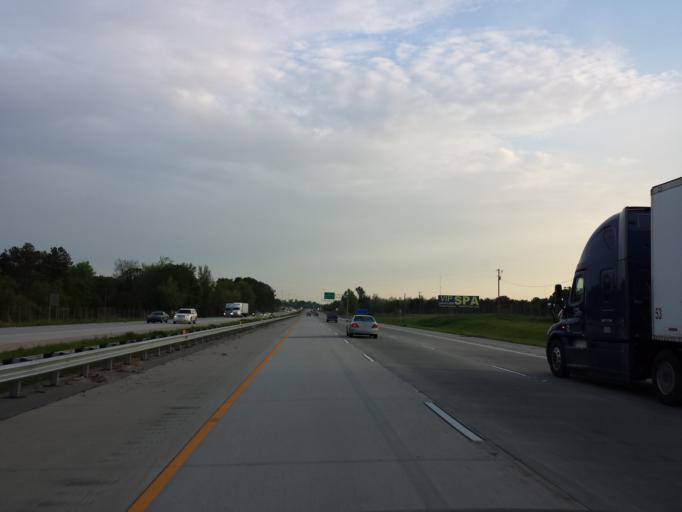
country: US
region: Georgia
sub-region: Dooly County
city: Unadilla
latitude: 32.2039
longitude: -83.7465
